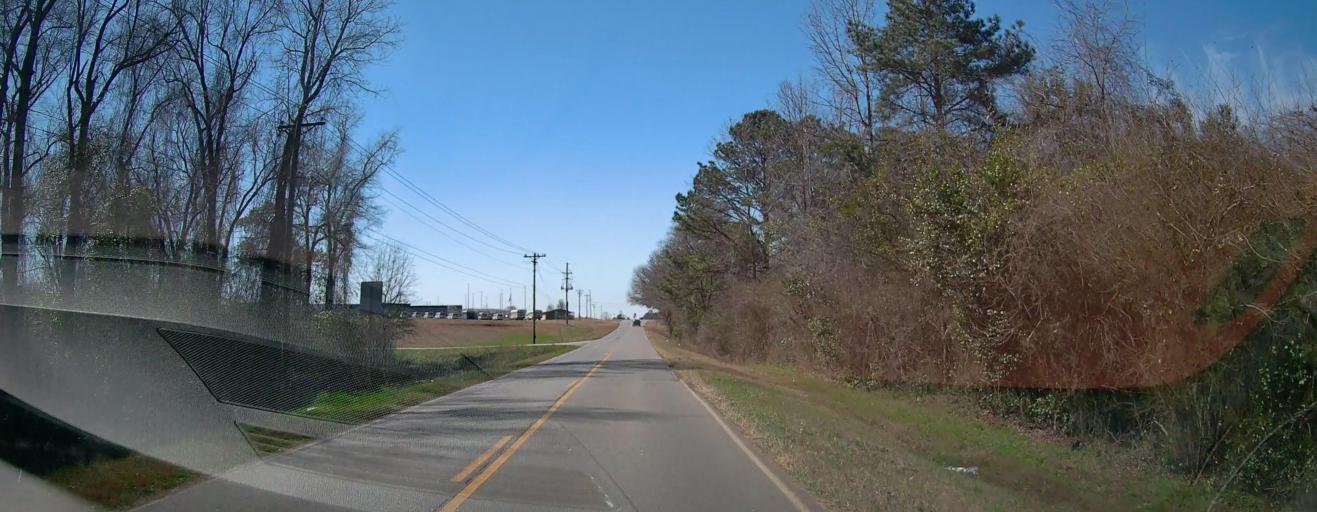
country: US
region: Georgia
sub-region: Houston County
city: Perry
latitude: 32.4659
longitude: -83.6921
